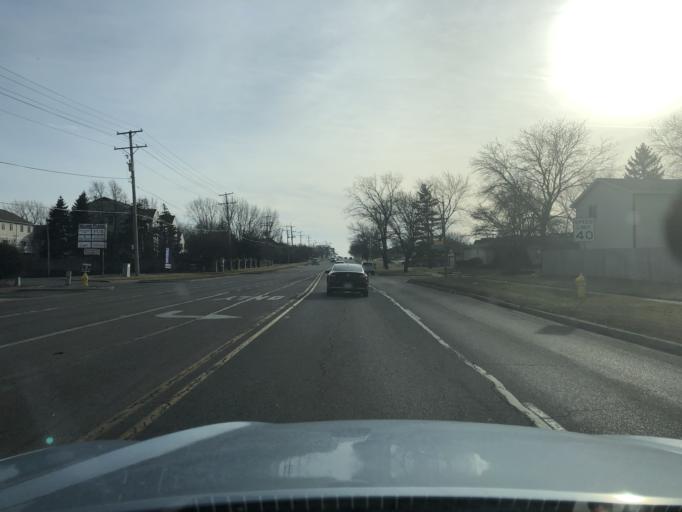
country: US
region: Illinois
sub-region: DuPage County
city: Glendale Heights
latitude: 41.9242
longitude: -88.0811
